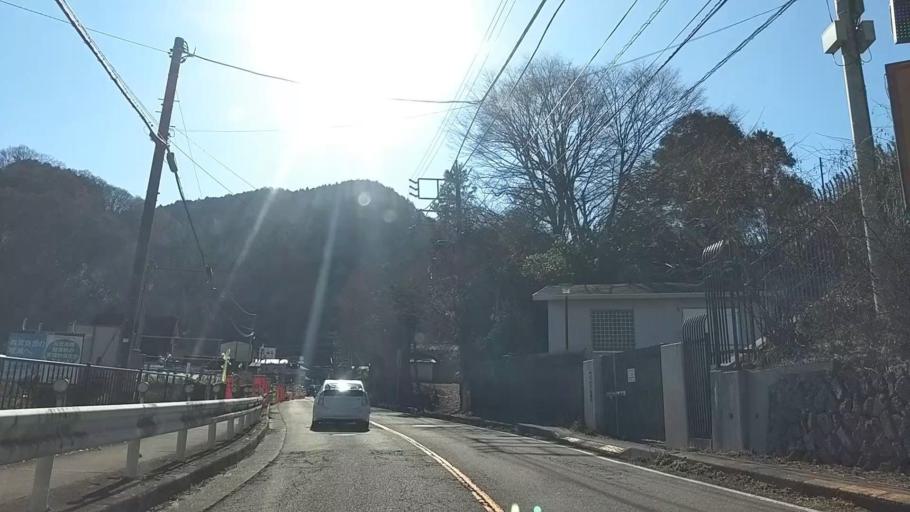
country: JP
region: Tokyo
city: Hachioji
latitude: 35.6201
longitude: 139.2624
